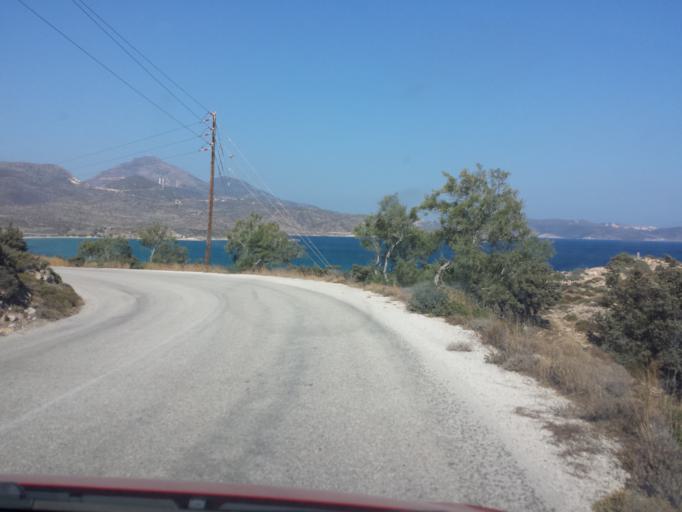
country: GR
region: South Aegean
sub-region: Nomos Kykladon
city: Adamas
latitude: 36.6936
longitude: 24.4575
